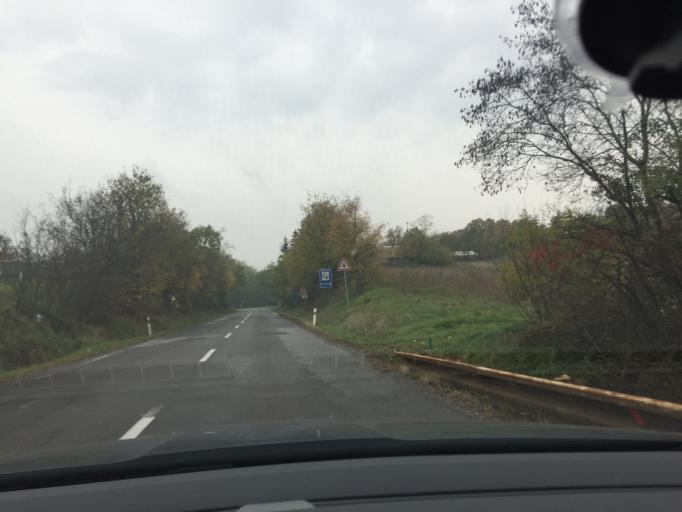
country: SK
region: Banskobystricky
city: Velky Krtis
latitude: 48.2672
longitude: 19.4466
